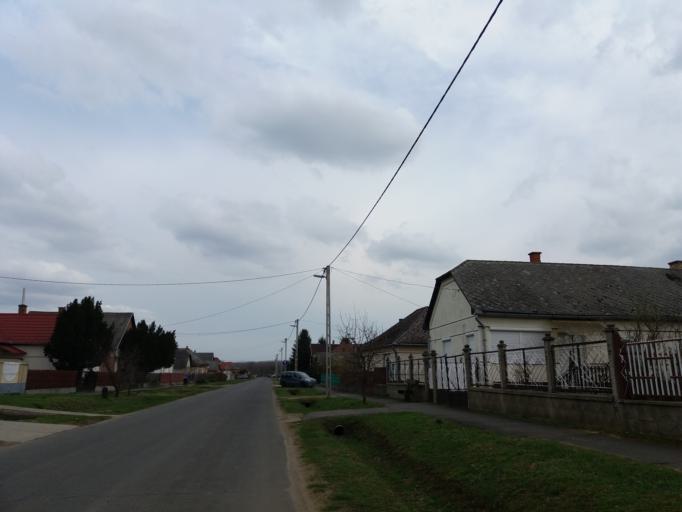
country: HU
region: Szabolcs-Szatmar-Bereg
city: Nyirtass
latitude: 48.1150
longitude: 22.0331
